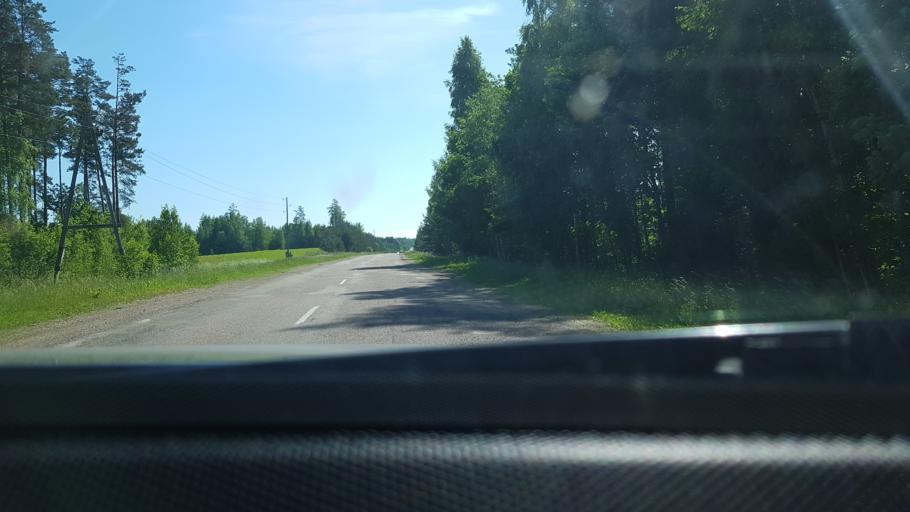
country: LV
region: Kraslavas Rajons
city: Kraslava
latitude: 55.8633
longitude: 26.9873
